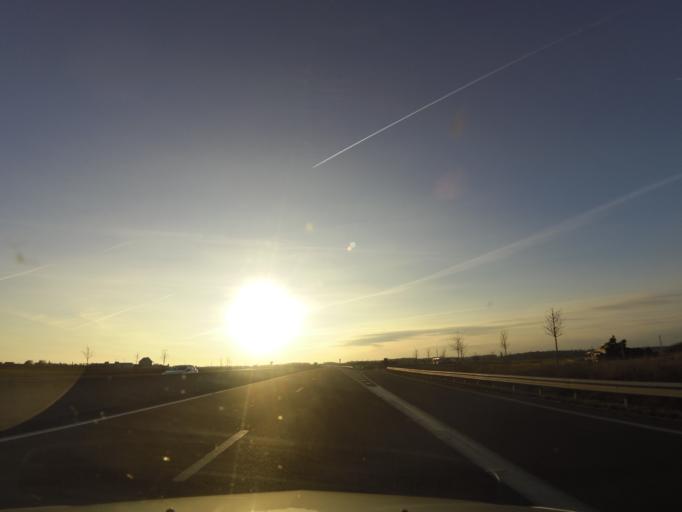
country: FR
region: Centre
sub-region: Departement du Loiret
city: Cepoy
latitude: 48.0586
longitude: 2.7375
